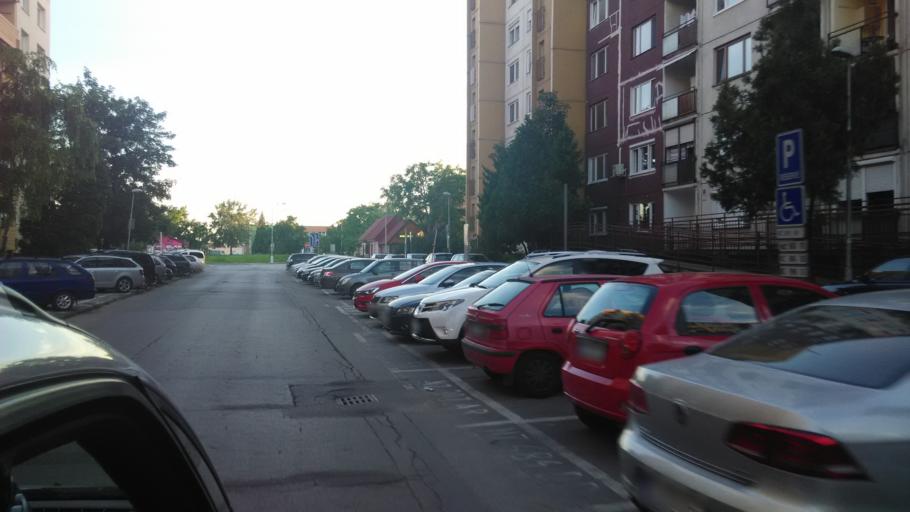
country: SK
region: Nitriansky
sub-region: Okres Nove Zamky
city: Nove Zamky
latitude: 47.9815
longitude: 18.1553
